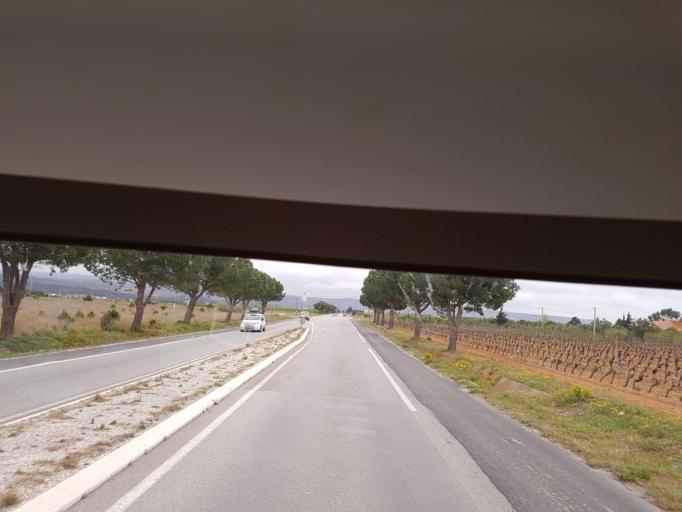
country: FR
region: Languedoc-Roussillon
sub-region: Departement des Pyrenees-Orientales
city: Salses-le-Chateau
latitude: 42.8077
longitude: 2.9123
